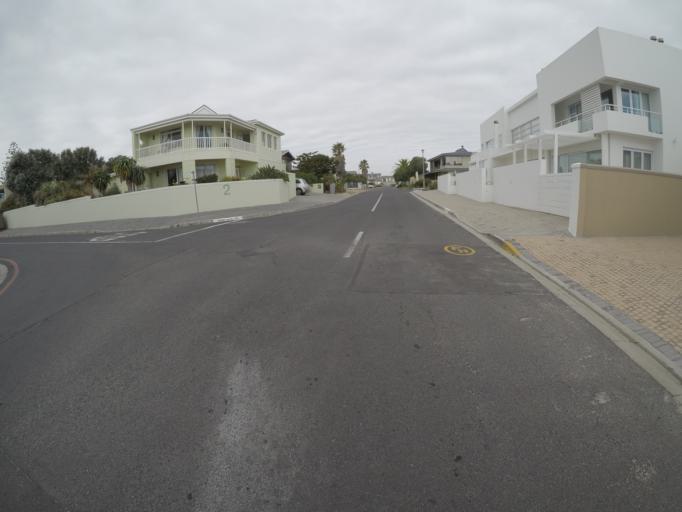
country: ZA
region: Western Cape
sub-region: City of Cape Town
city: Sunset Beach
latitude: -33.7202
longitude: 18.4448
